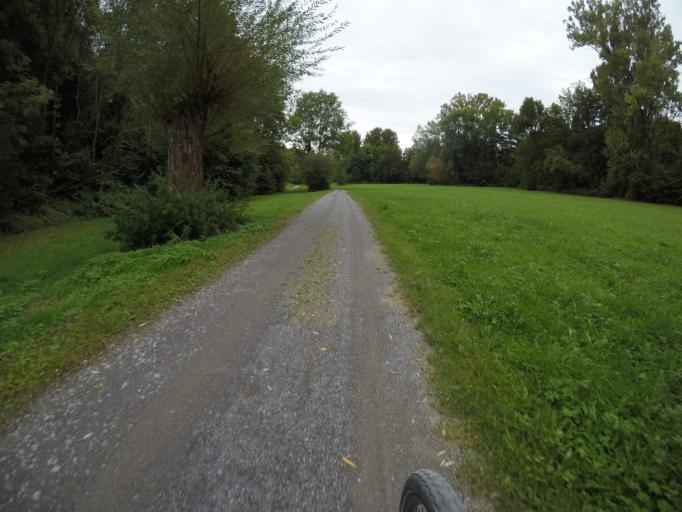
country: DE
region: Baden-Wuerttemberg
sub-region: Regierungsbezirk Stuttgart
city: Eberdingen
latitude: 48.9004
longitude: 8.9791
